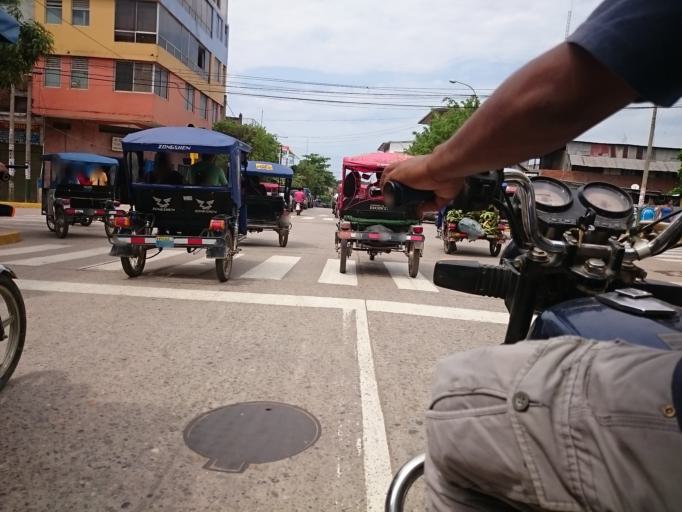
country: PE
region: Ucayali
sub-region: Provincia de Coronel Portillo
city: Pucallpa
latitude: -8.3871
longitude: -74.5309
